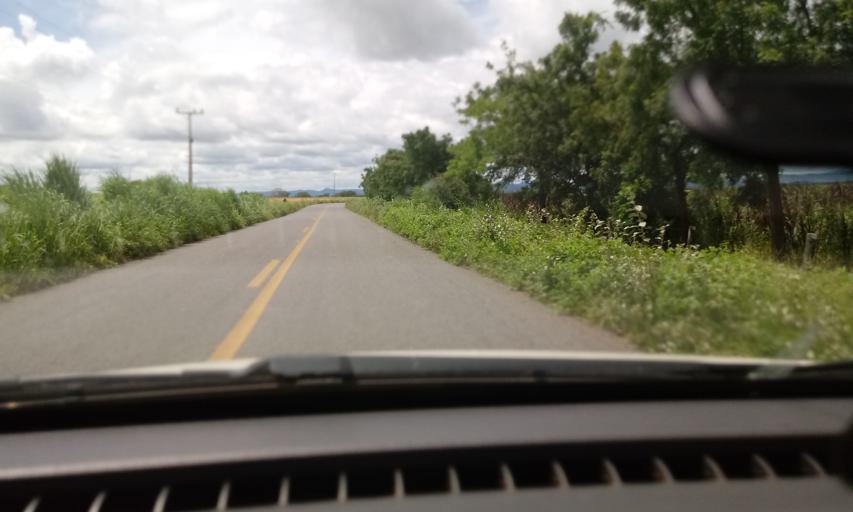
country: BR
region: Bahia
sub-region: Guanambi
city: Guanambi
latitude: -14.0538
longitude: -42.8749
